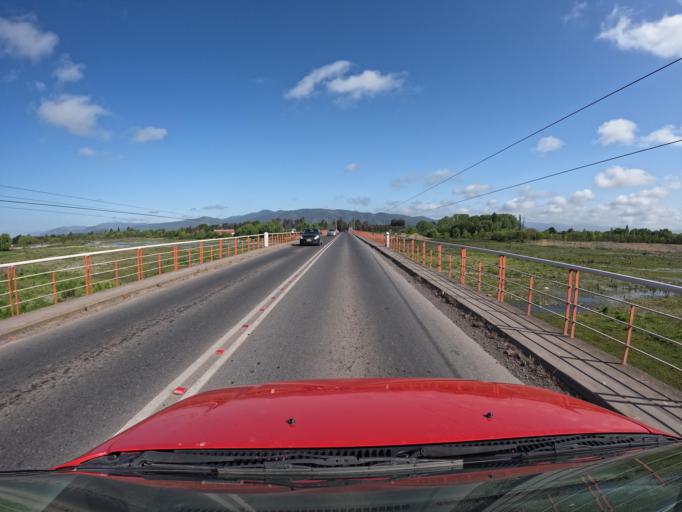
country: CL
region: Maule
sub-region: Provincia de Curico
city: Rauco
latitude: -34.9345
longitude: -71.2735
